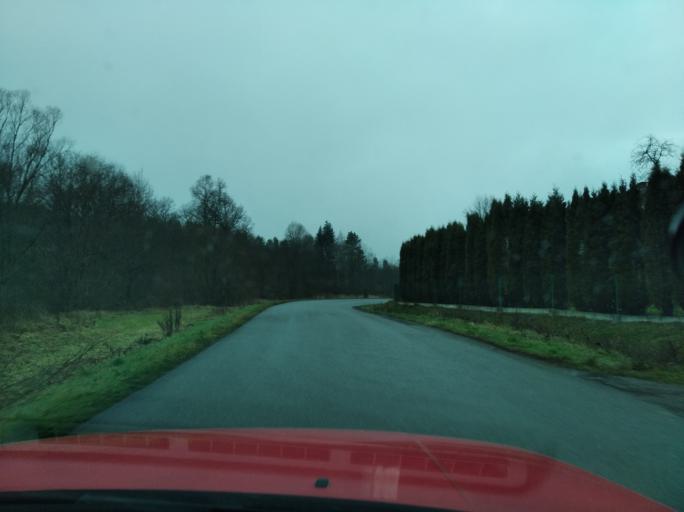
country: PL
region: Subcarpathian Voivodeship
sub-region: Powiat przemyski
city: Nienadowa
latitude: 49.8677
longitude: 22.4196
